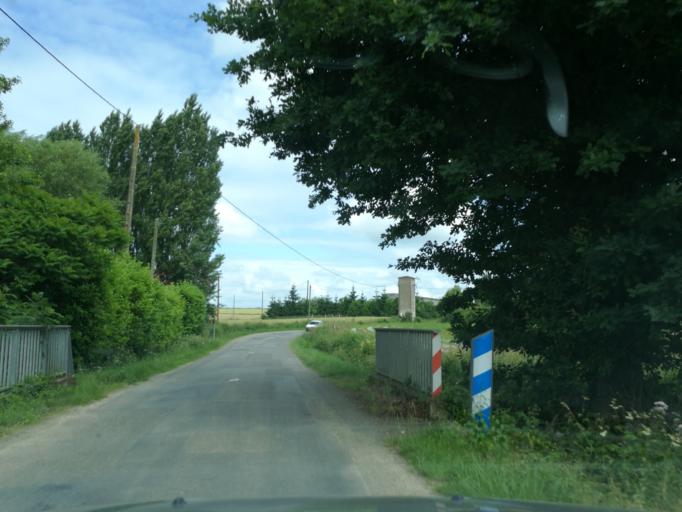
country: FR
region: Brittany
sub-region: Departement d'Ille-et-Vilaine
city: Bedee
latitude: 48.1812
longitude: -1.9849
